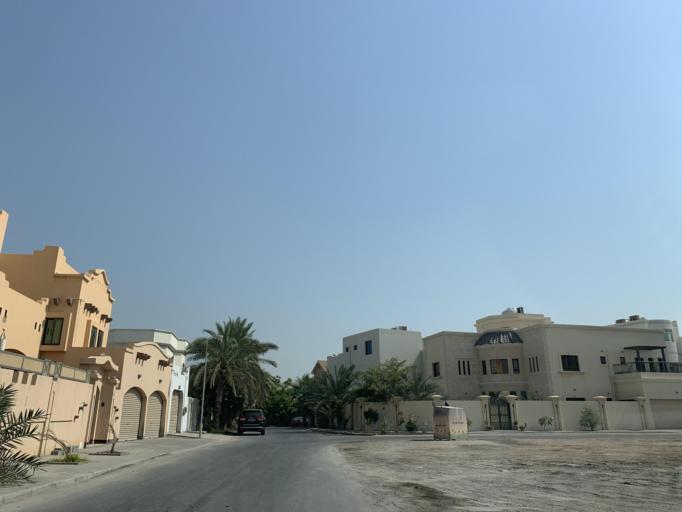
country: BH
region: Northern
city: Madinat `Isa
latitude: 26.1951
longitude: 50.5125
